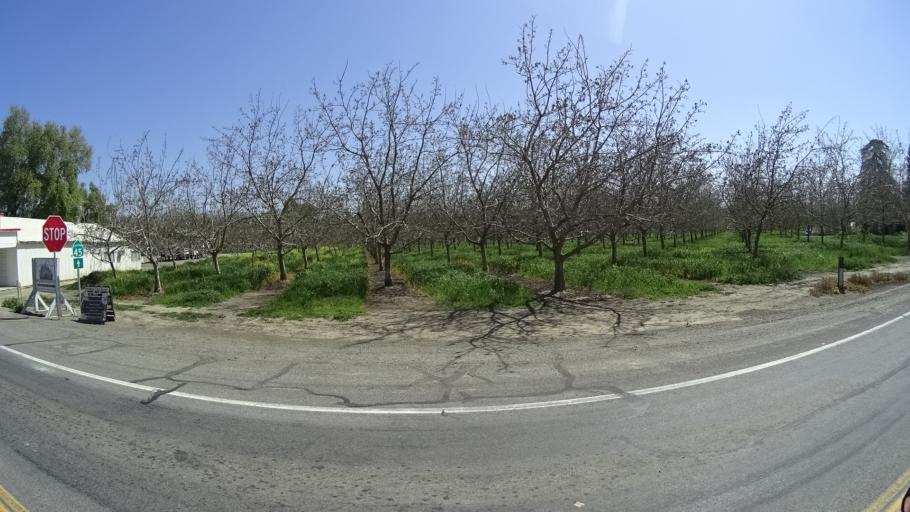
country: US
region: California
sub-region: Glenn County
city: Willows
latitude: 39.5216
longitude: -122.0141
